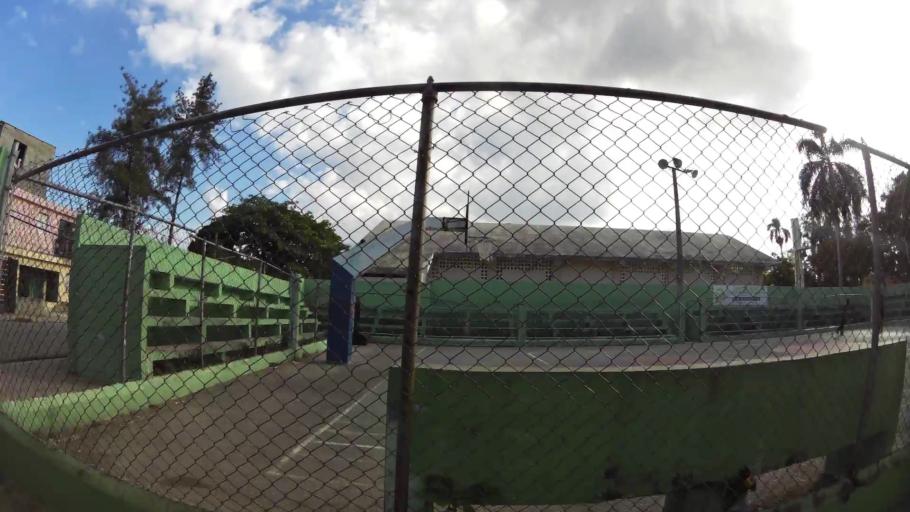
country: DO
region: Nacional
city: Ensanche Luperon
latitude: 18.5518
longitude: -69.8994
